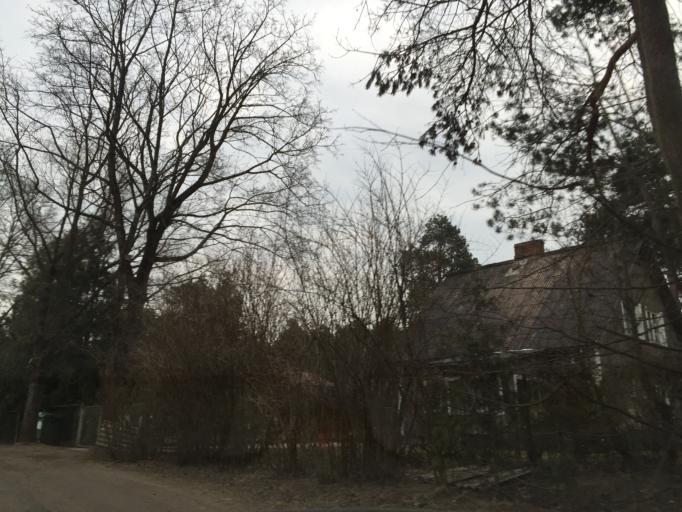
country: LV
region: Riga
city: Bergi
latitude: 56.9979
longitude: 24.2820
